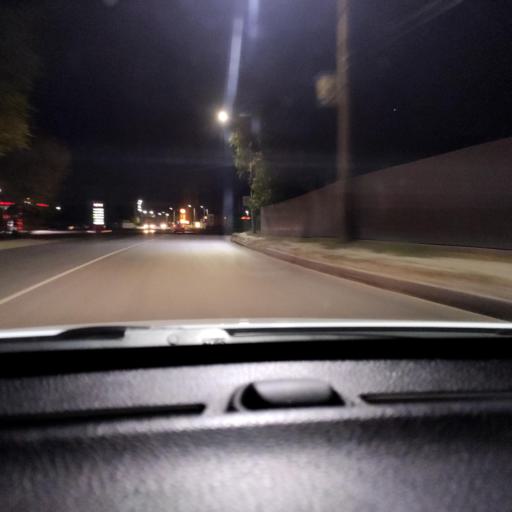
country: RU
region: Voronezj
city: Maslovka
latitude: 51.6296
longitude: 39.2619
